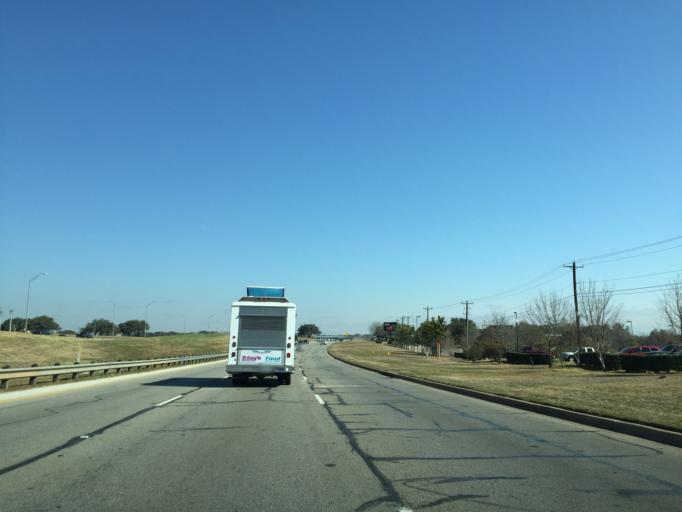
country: US
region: Texas
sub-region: Williamson County
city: Georgetown
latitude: 30.6416
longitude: -97.6870
